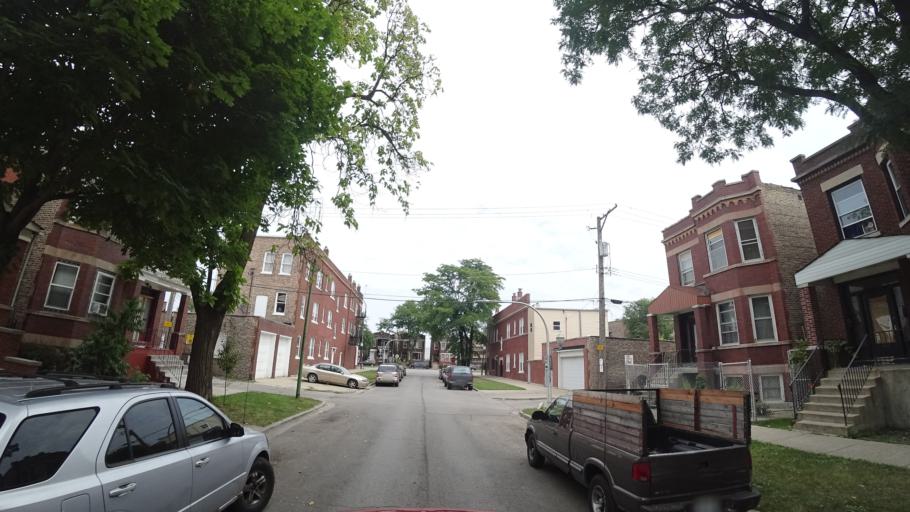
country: US
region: Illinois
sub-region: Cook County
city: Cicero
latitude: 41.8507
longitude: -87.7335
